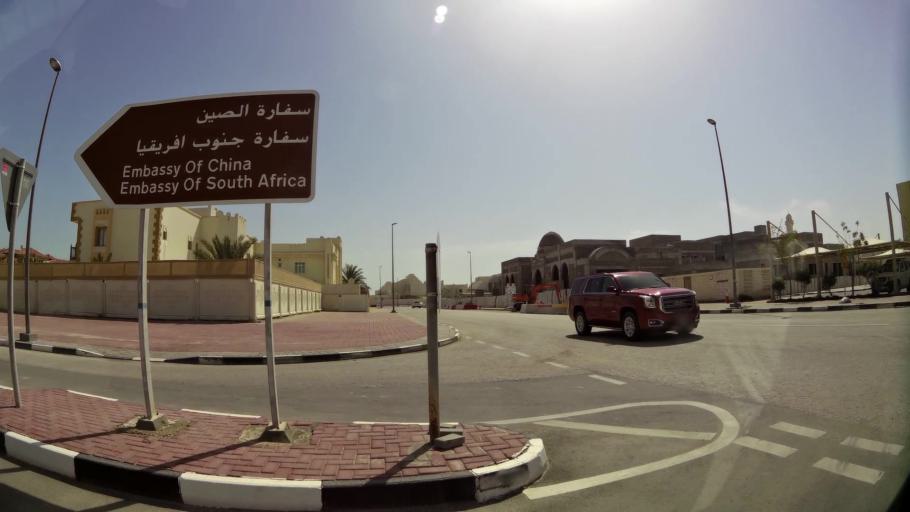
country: QA
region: Baladiyat ad Dawhah
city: Doha
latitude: 25.3601
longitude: 51.5013
